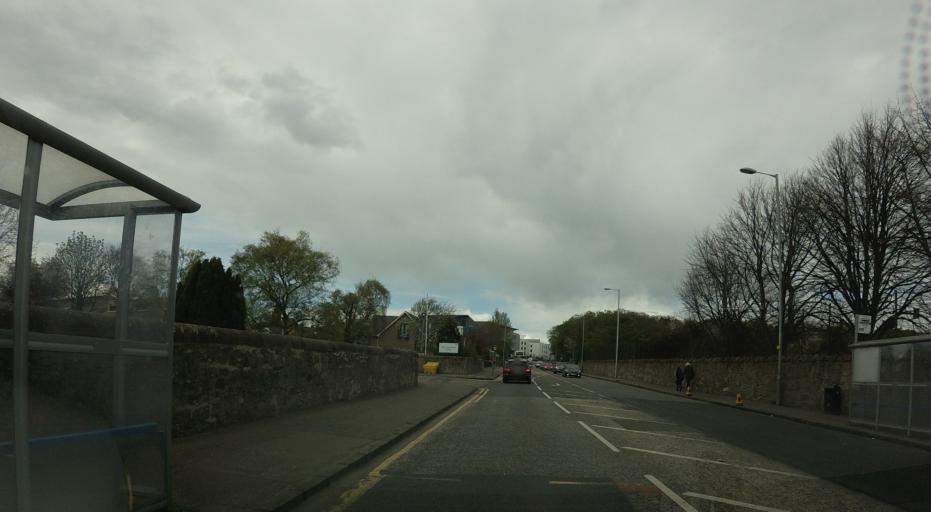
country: GB
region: Scotland
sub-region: Edinburgh
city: Edinburgh
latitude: 55.9601
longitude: -3.2285
